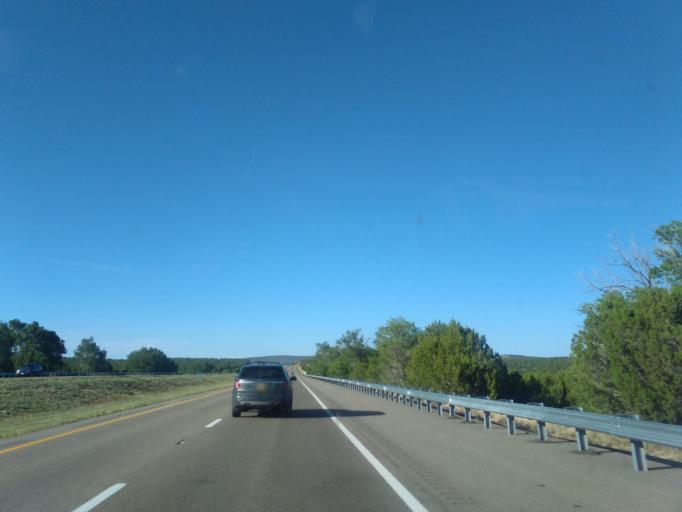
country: US
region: New Mexico
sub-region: San Miguel County
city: Las Vegas
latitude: 35.4363
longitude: -105.2896
